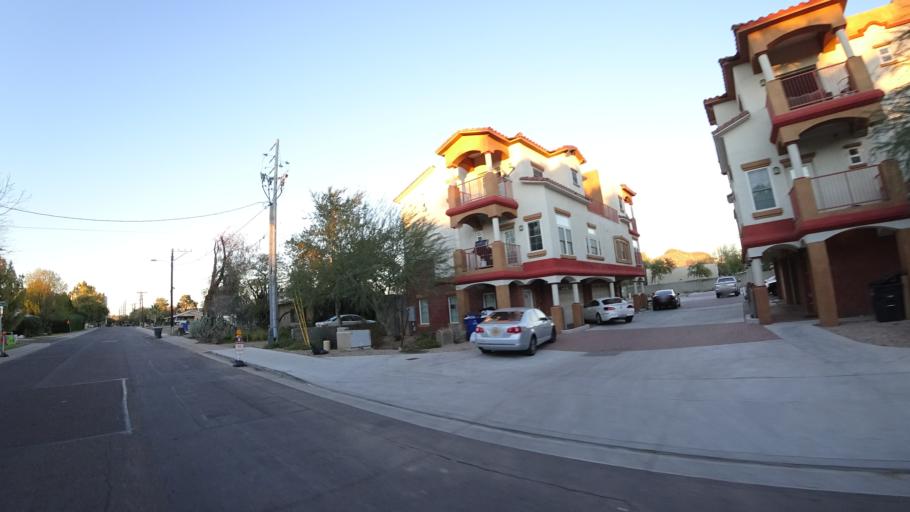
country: US
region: Arizona
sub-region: Maricopa County
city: Tempe Junction
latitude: 33.4268
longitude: -111.9473
